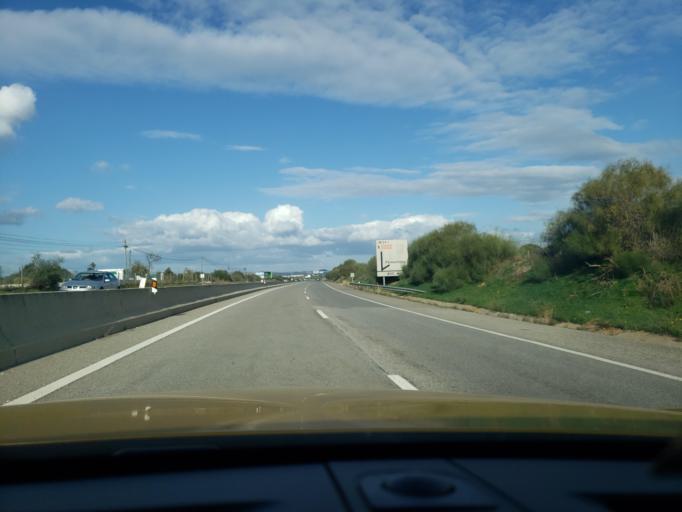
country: PT
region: Faro
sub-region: Lagoa
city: Lagoa
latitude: 37.1550
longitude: -8.4503
